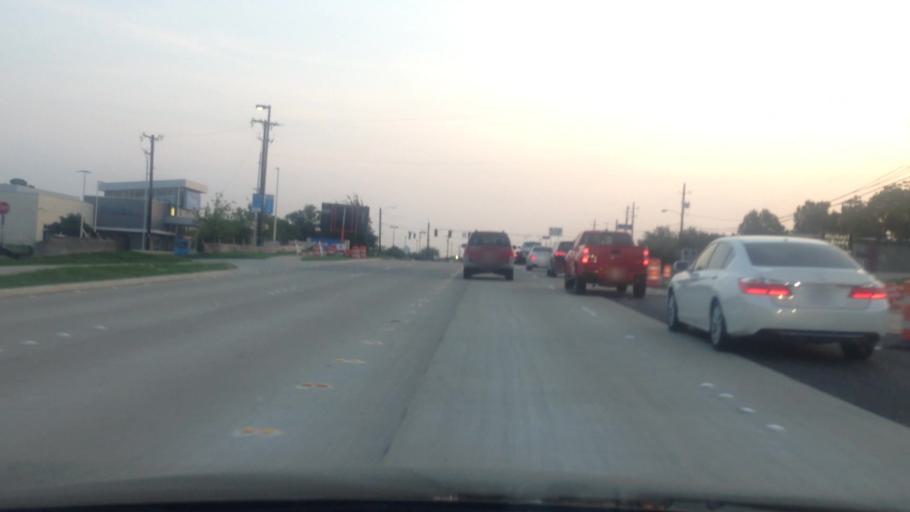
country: US
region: Texas
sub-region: Tarrant County
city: Colleyville
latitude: 32.8875
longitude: -97.1513
